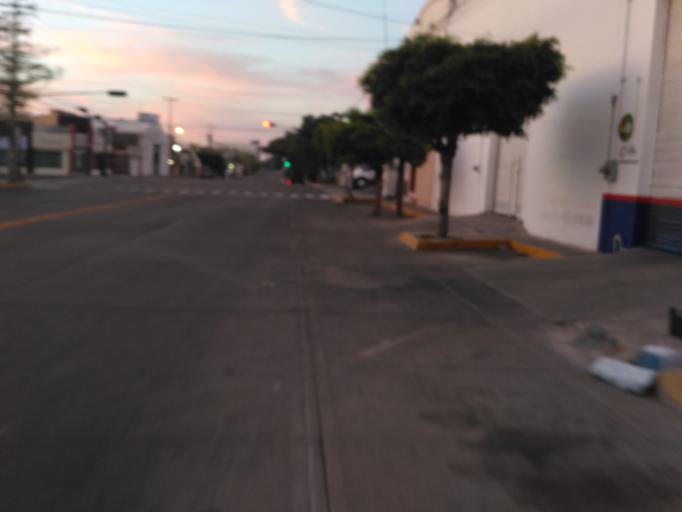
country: MX
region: Sinaloa
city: Culiacan
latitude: 24.7986
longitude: -107.4043
